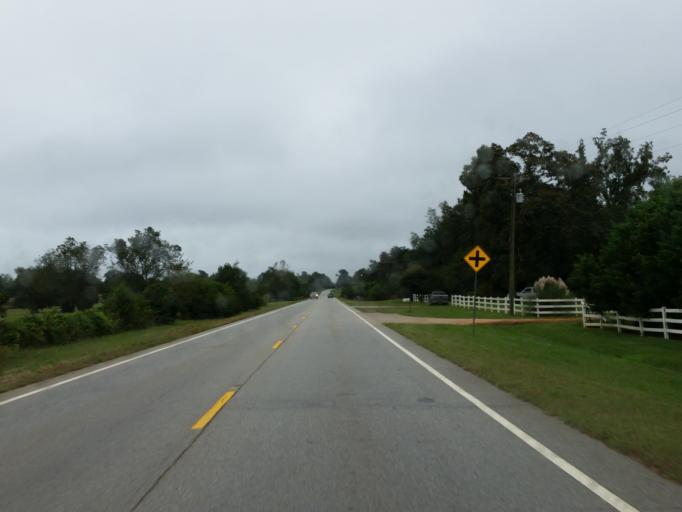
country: US
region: Georgia
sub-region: Lamar County
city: Barnesville
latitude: 32.9768
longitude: -84.1151
